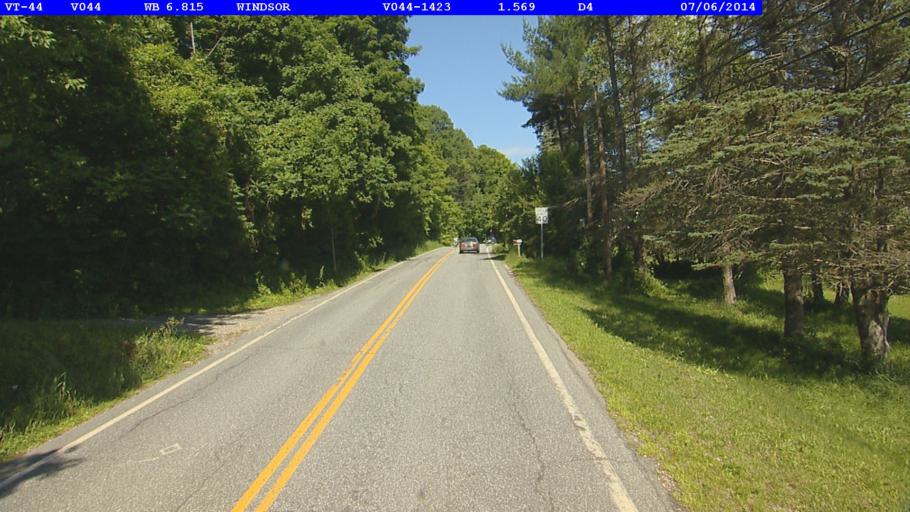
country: US
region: Vermont
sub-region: Windsor County
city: Windsor
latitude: 43.4596
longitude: -72.4249
